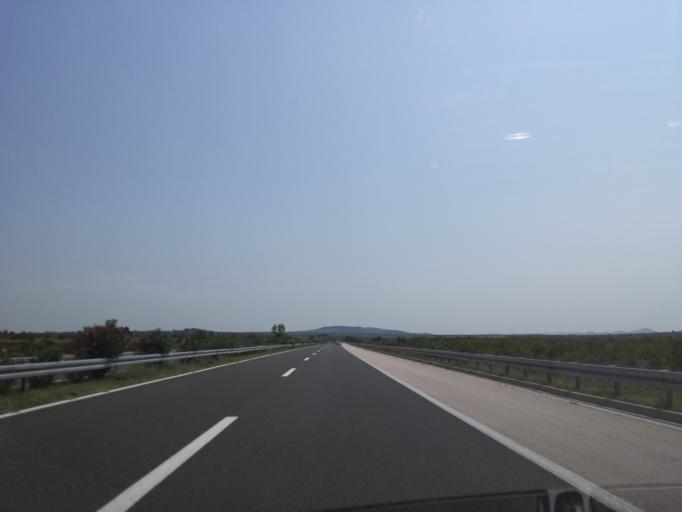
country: HR
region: Zadarska
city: Galovac
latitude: 44.1070
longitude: 15.4572
